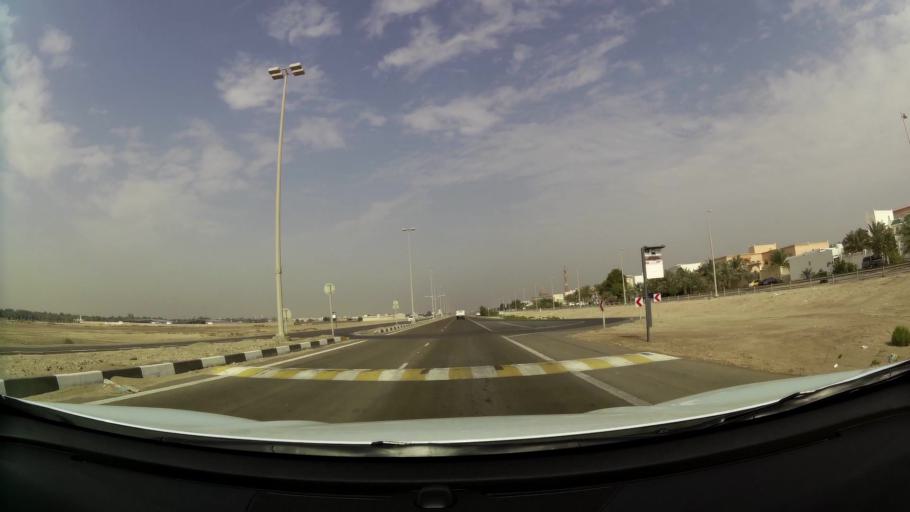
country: AE
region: Abu Dhabi
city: Abu Dhabi
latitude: 24.2807
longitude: 54.6609
